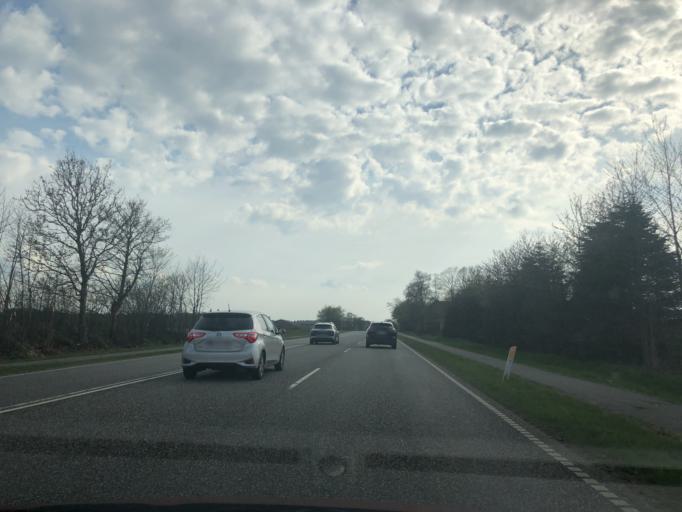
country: DK
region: Zealand
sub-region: Lejre Kommune
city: Osted
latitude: 55.5265
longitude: 11.9095
